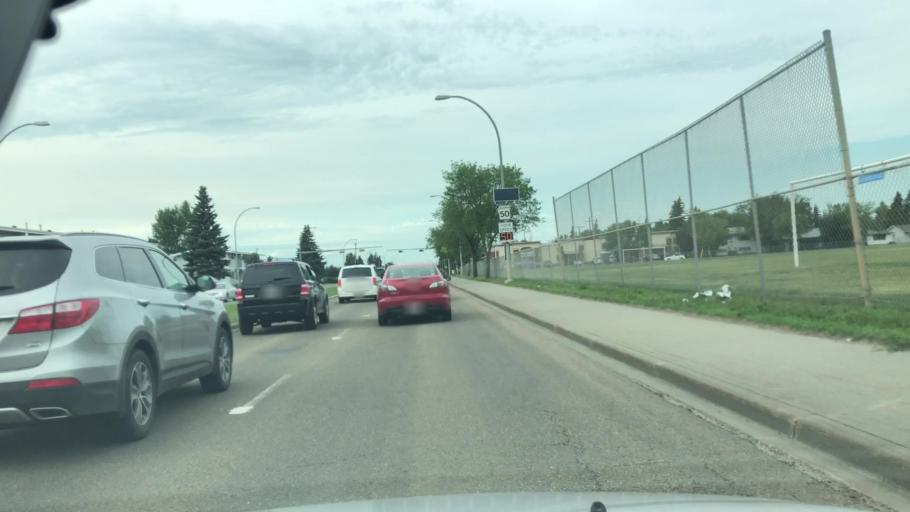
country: CA
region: Alberta
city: Edmonton
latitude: 53.5933
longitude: -113.5165
